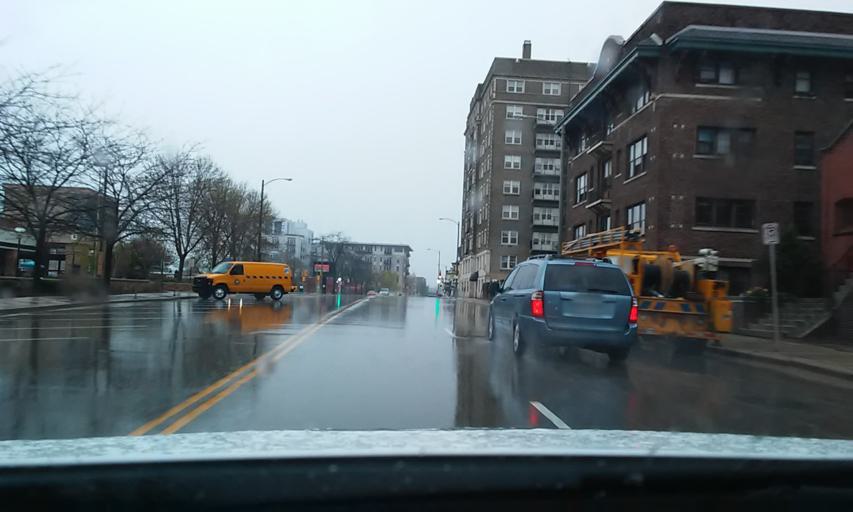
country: US
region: Wisconsin
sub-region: Milwaukee County
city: Milwaukee
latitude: 43.0446
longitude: -87.9034
